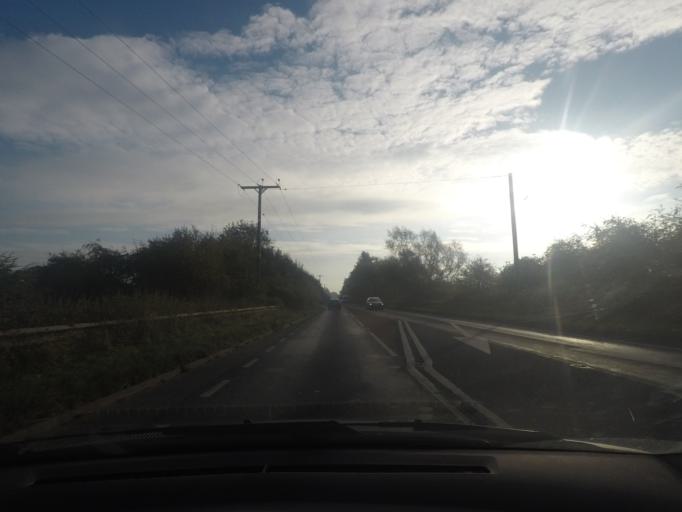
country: GB
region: England
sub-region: East Riding of Yorkshire
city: Wilberfoss
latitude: 53.9478
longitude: -0.8957
